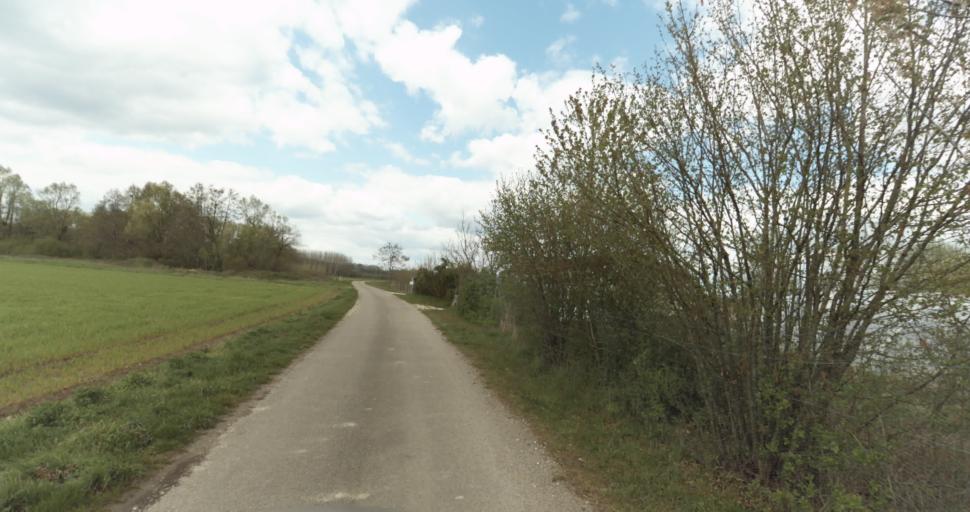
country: FR
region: Bourgogne
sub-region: Departement de la Cote-d'Or
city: Auxonne
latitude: 47.1661
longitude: 5.3950
